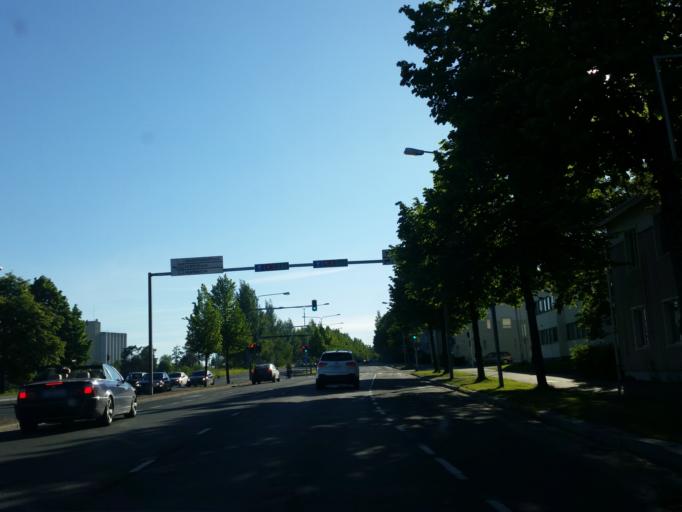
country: FI
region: Northern Savo
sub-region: Kuopio
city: Kuopio
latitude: 62.8821
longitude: 27.6654
